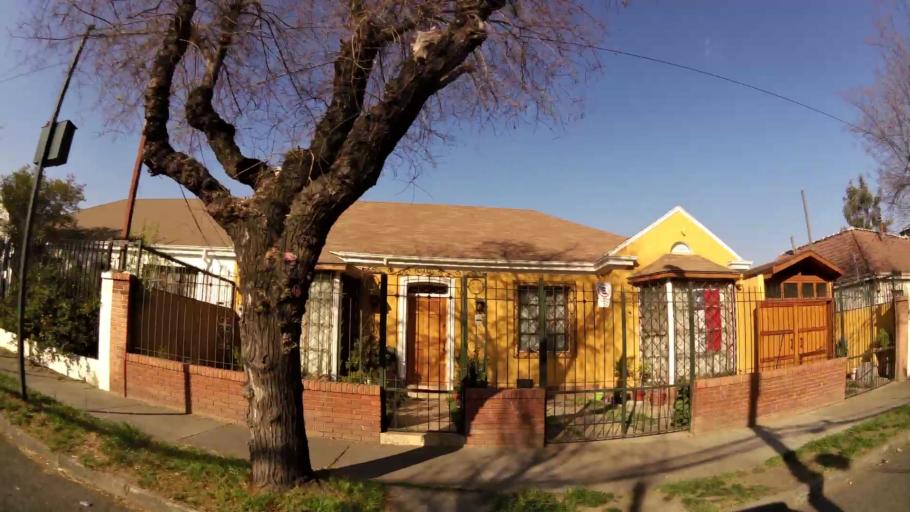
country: CL
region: Santiago Metropolitan
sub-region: Provincia de Santiago
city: Villa Presidente Frei, Nunoa, Santiago, Chile
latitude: -33.4507
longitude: -70.6016
